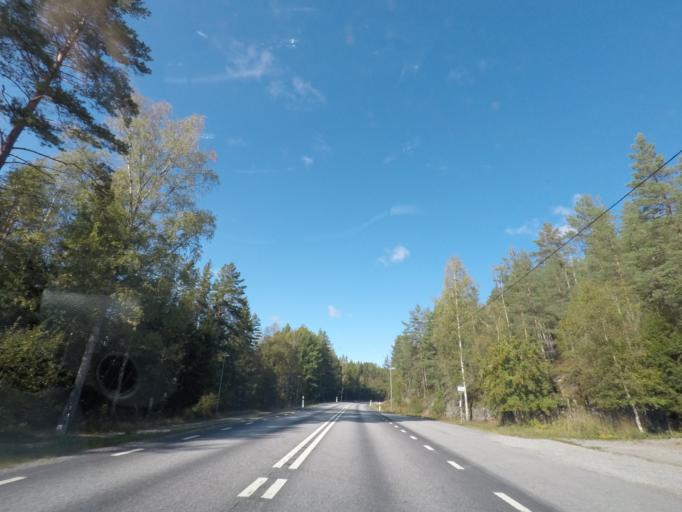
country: SE
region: Vaestmanland
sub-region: Skinnskattebergs Kommun
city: Skinnskatteberg
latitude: 59.8221
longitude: 15.5324
